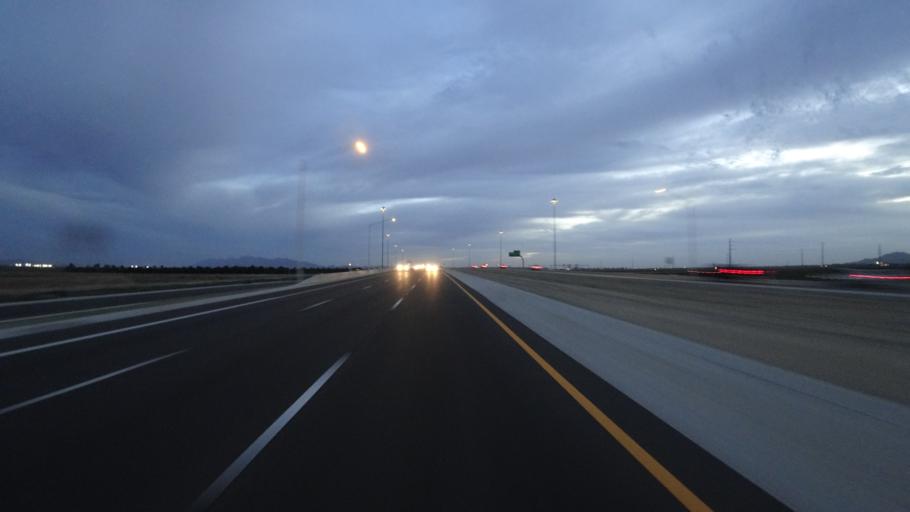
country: US
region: Arizona
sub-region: Maricopa County
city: Citrus Park
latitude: 33.5257
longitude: -112.4185
